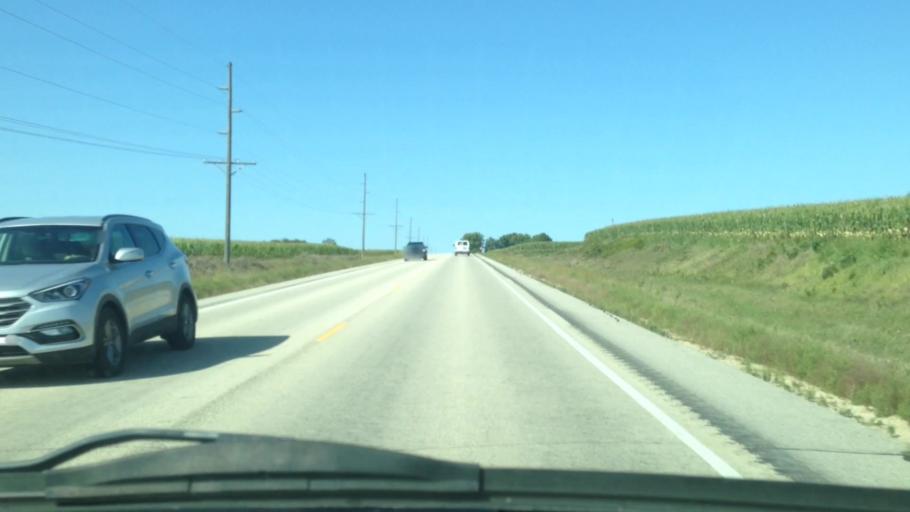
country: US
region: Minnesota
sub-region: Fillmore County
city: Rushford
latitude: 43.9135
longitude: -91.7401
